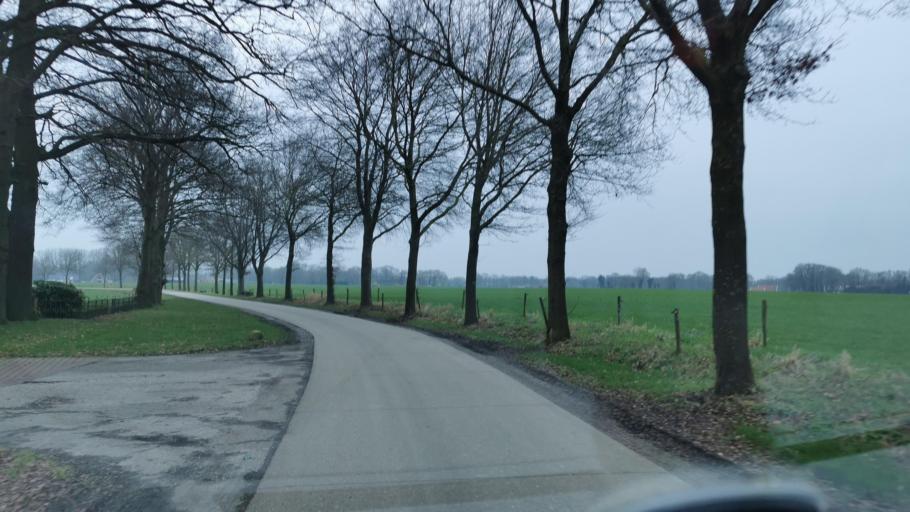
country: NL
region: Overijssel
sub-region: Gemeente Tubbergen
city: Tubbergen
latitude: 52.3471
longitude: 6.7984
